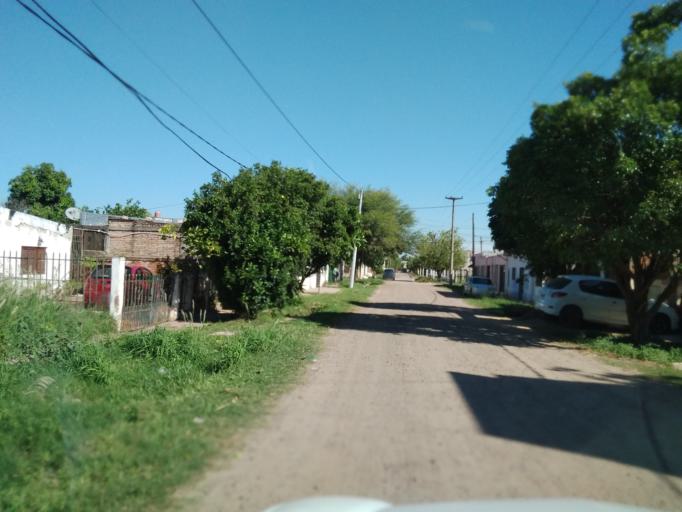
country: AR
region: Corrientes
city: Corrientes
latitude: -27.4841
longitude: -58.8059
